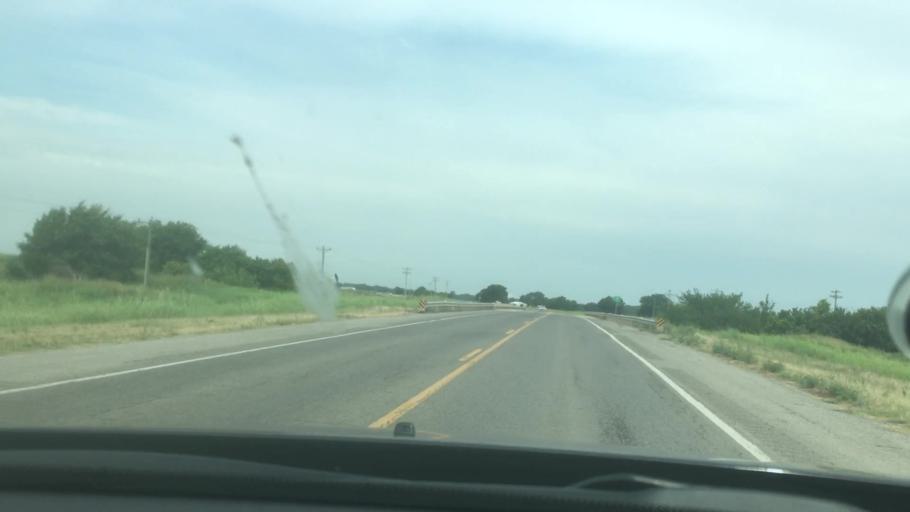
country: US
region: Oklahoma
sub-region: Garvin County
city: Maysville
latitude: 34.8202
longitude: -97.4915
